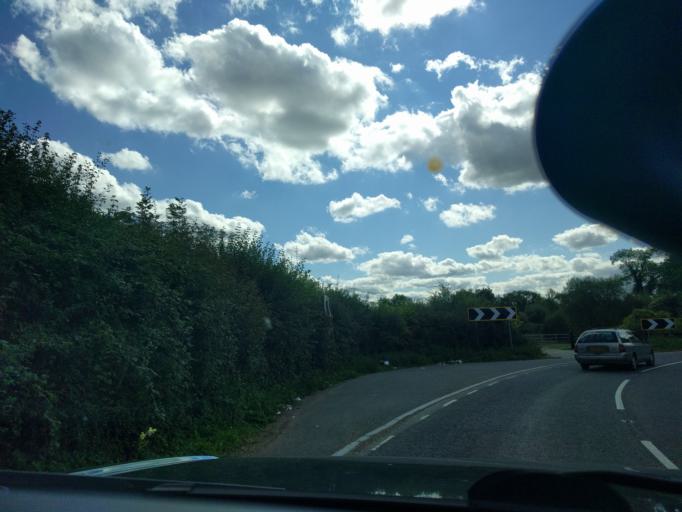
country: GB
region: England
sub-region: Wiltshire
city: Bradford-on-Avon
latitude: 51.3712
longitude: -2.2353
